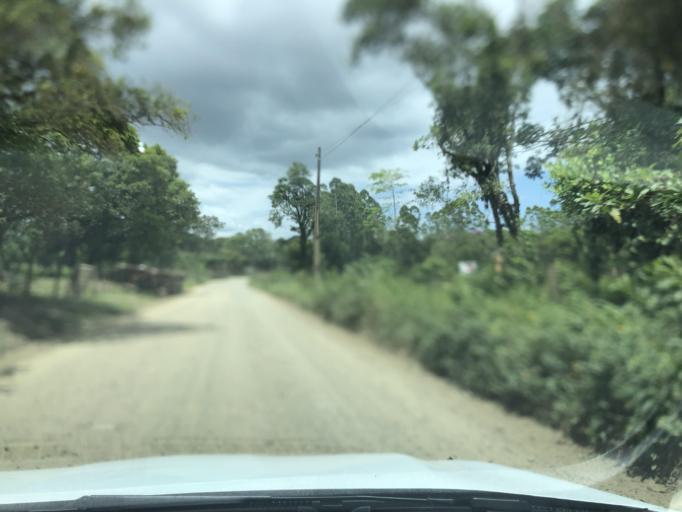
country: BR
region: Santa Catarina
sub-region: Sao Francisco Do Sul
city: Sao Francisco do Sul
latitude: -26.2252
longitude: -48.5792
